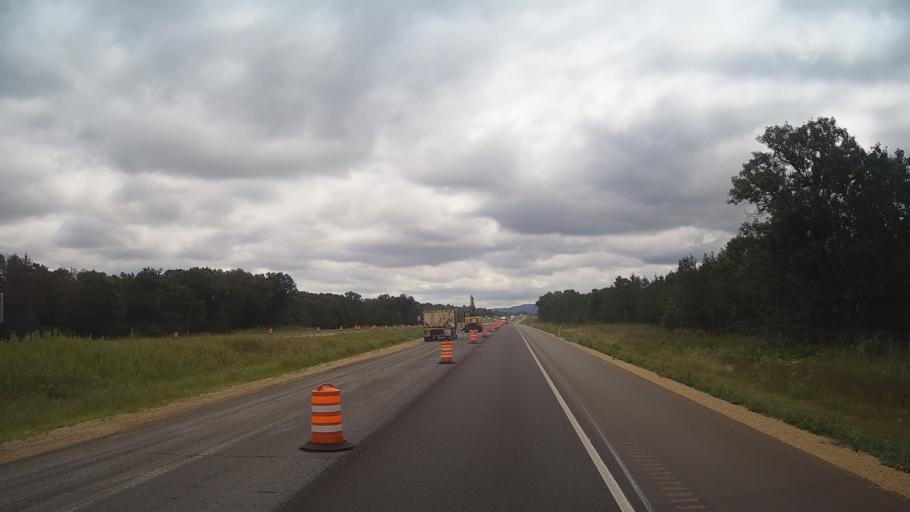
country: US
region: Wisconsin
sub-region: Monroe County
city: Sparta
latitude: 43.9434
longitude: -90.7422
